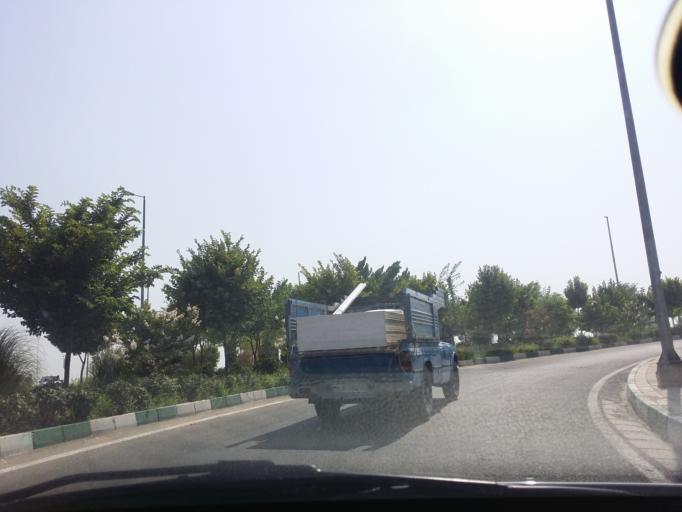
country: IR
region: Alborz
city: Karaj
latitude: 35.7899
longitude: 51.0044
